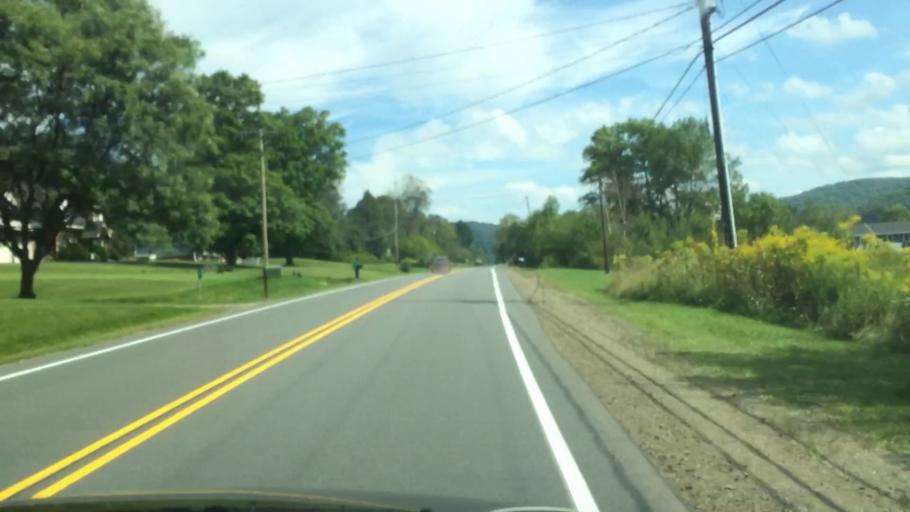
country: US
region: Pennsylvania
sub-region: McKean County
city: Bradford
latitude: 41.9119
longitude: -78.6368
